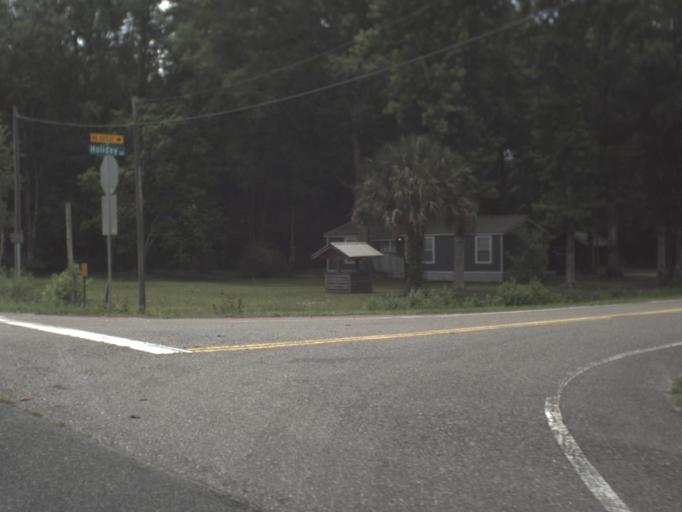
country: US
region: Florida
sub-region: Nassau County
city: Hilliard
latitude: 30.6517
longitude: -81.8750
